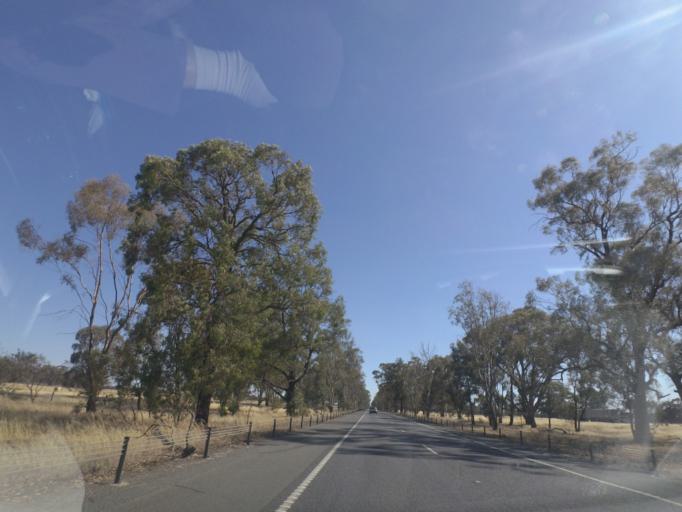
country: AU
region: Victoria
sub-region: Greater Shepparton
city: Shepparton
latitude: -36.5913
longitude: 145.3318
